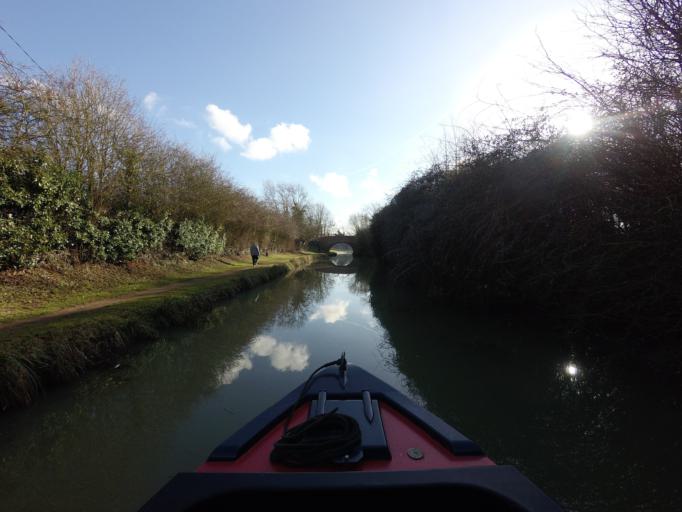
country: GB
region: England
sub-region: Northamptonshire
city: Blisworth
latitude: 52.1959
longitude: -0.9438
